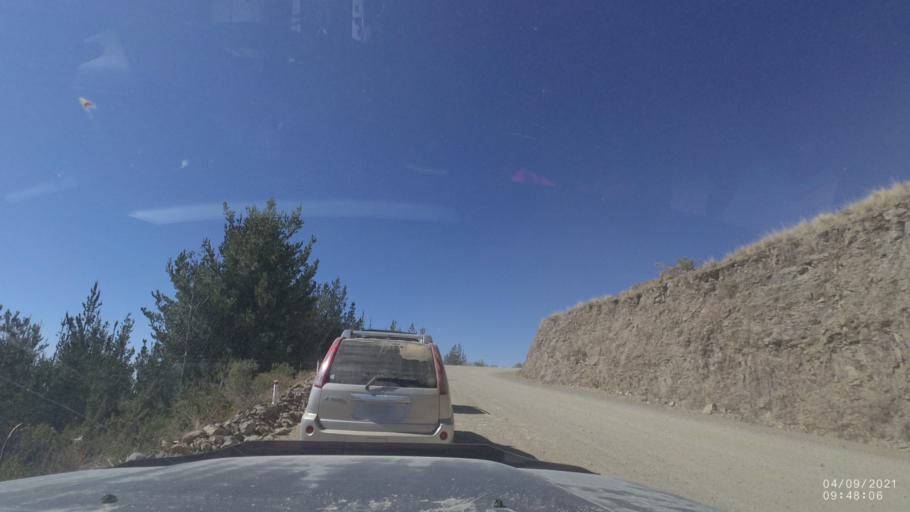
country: BO
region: Cochabamba
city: Sipe Sipe
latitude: -17.3548
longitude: -66.3871
